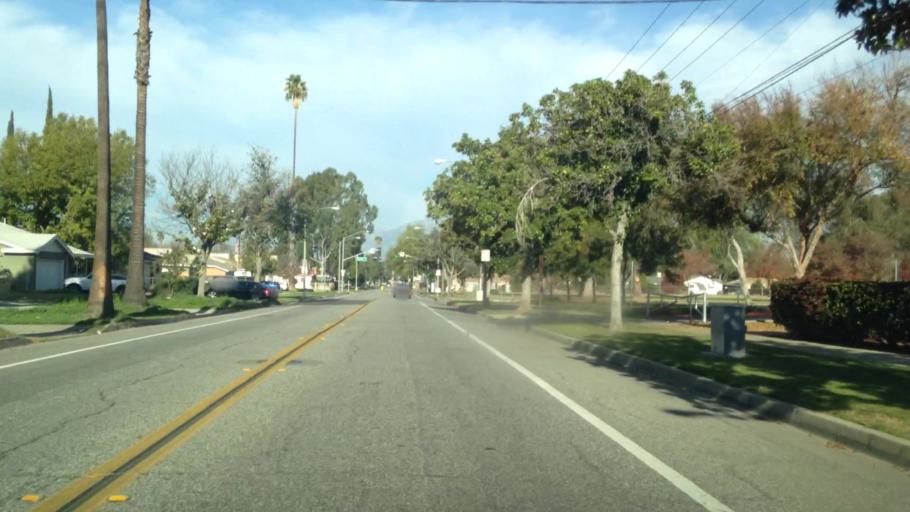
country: US
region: California
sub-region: Riverside County
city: Riverside
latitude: 33.9388
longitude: -117.4181
